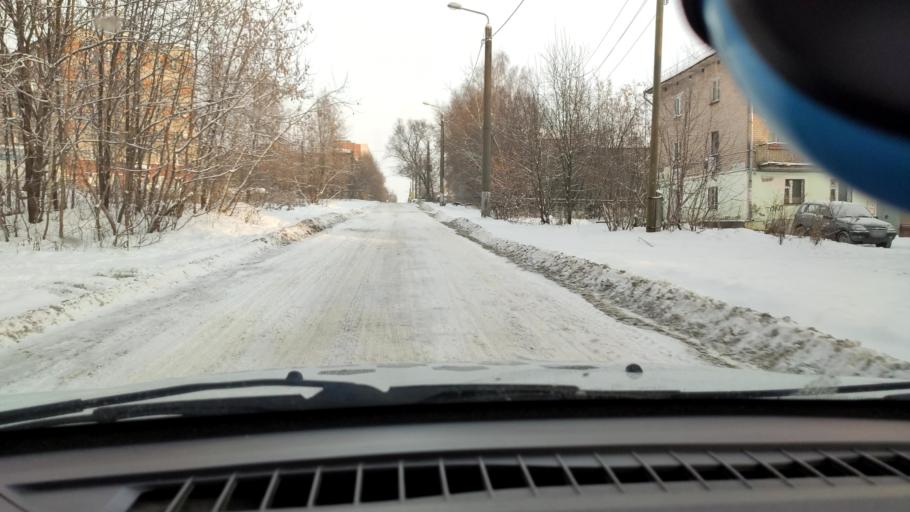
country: RU
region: Perm
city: Perm
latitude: 58.0976
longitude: 56.2905
